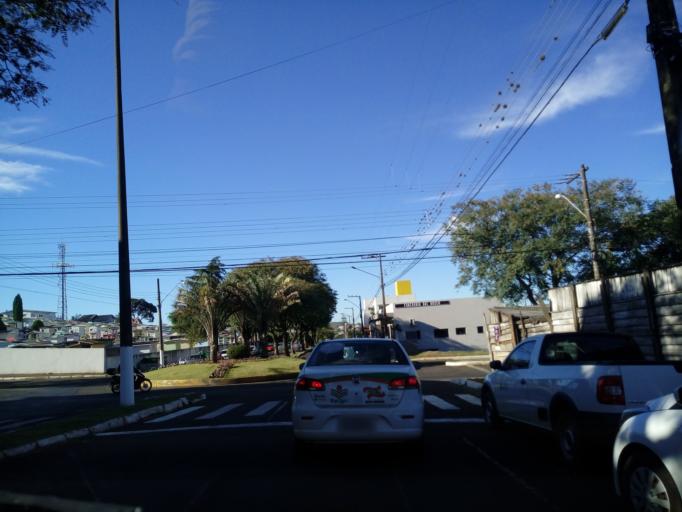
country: BR
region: Santa Catarina
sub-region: Chapeco
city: Chapeco
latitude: -27.1118
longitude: -52.6145
